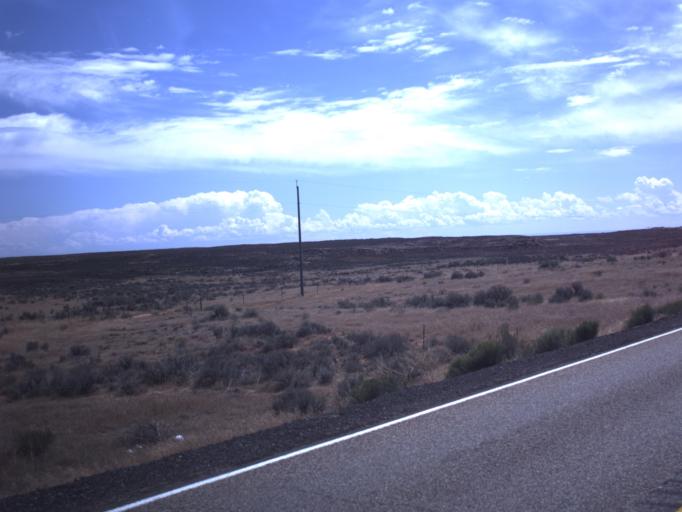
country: US
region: Utah
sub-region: Uintah County
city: Maeser
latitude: 40.2860
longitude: -109.6839
